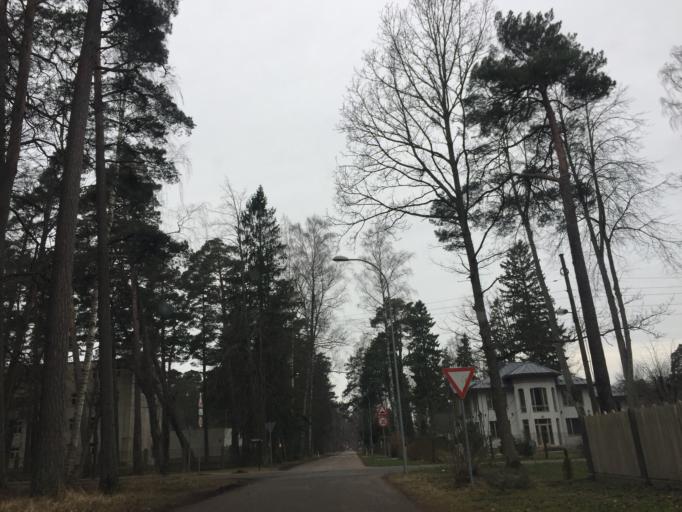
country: LV
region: Jurmala
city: Jurmala
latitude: 56.9620
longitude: 23.7374
